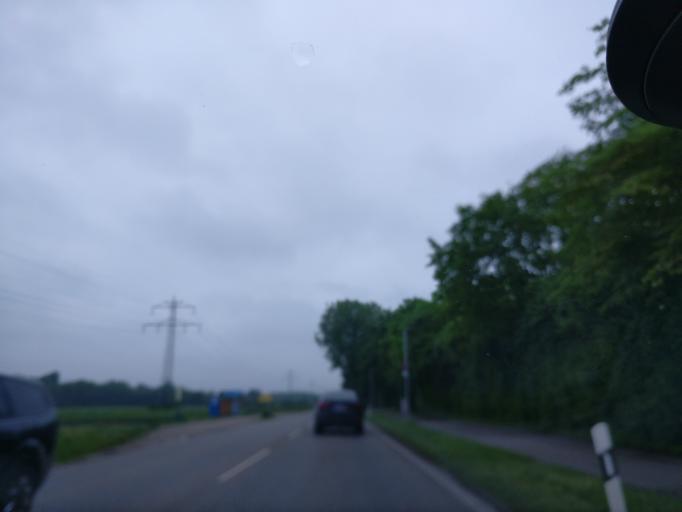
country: DE
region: Bavaria
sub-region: Upper Bavaria
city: Dachau
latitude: 48.2533
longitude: 11.4555
